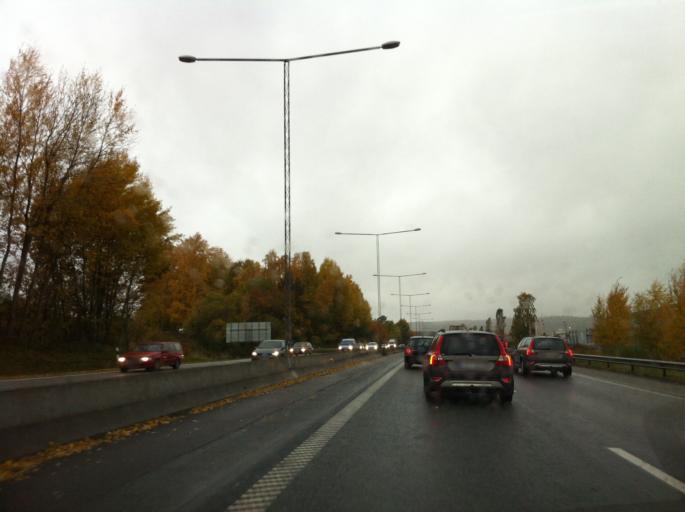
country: SE
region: Joenkoeping
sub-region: Jonkopings Kommun
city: Jonkoping
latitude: 57.7614
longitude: 14.1867
